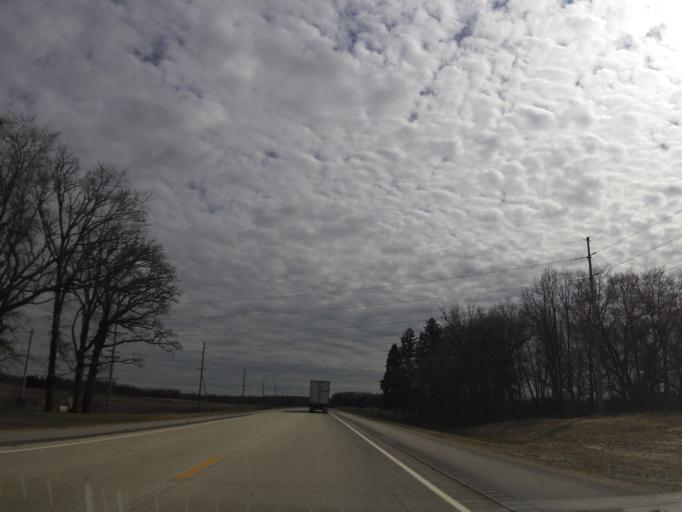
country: US
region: Minnesota
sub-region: Fillmore County
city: Spring Valley
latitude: 43.6363
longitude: -92.3895
